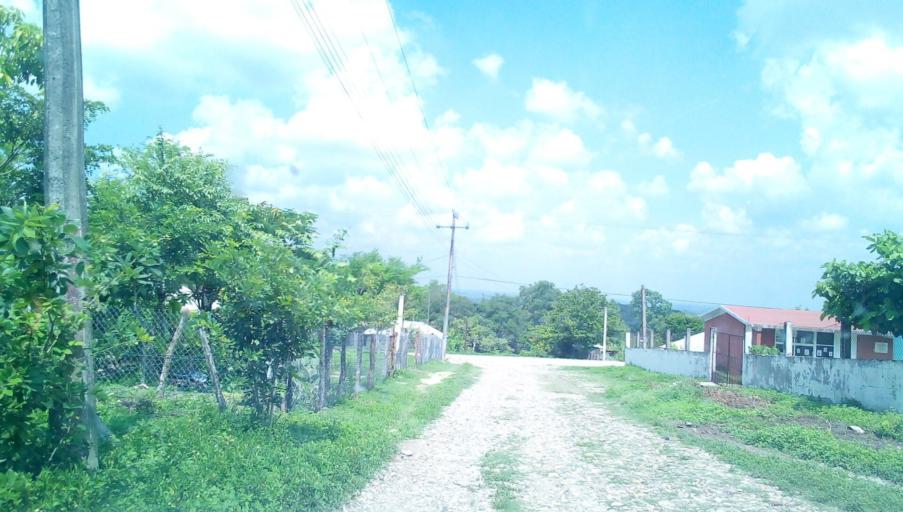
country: MX
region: Veracruz
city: Tempoal de Sanchez
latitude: 21.6053
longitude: -98.2913
